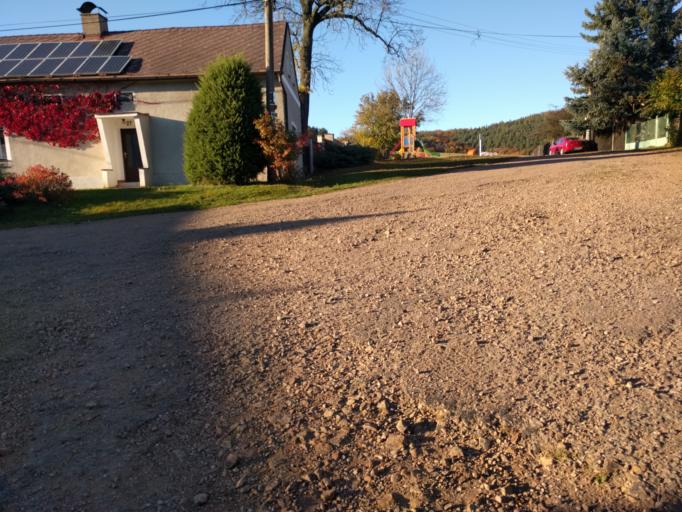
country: CZ
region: Plzensky
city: Zbiroh
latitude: 49.8923
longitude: 13.7215
